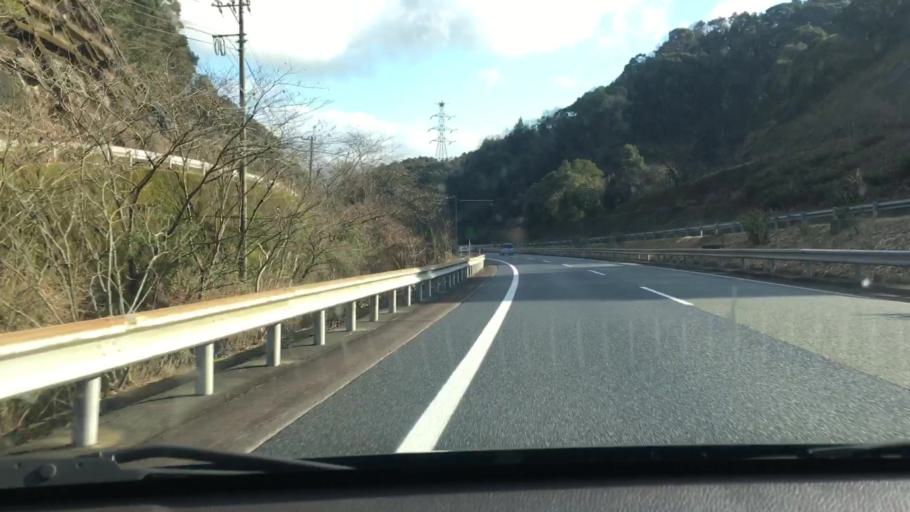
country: JP
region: Kumamoto
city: Hitoyoshi
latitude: 32.2693
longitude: 130.7609
